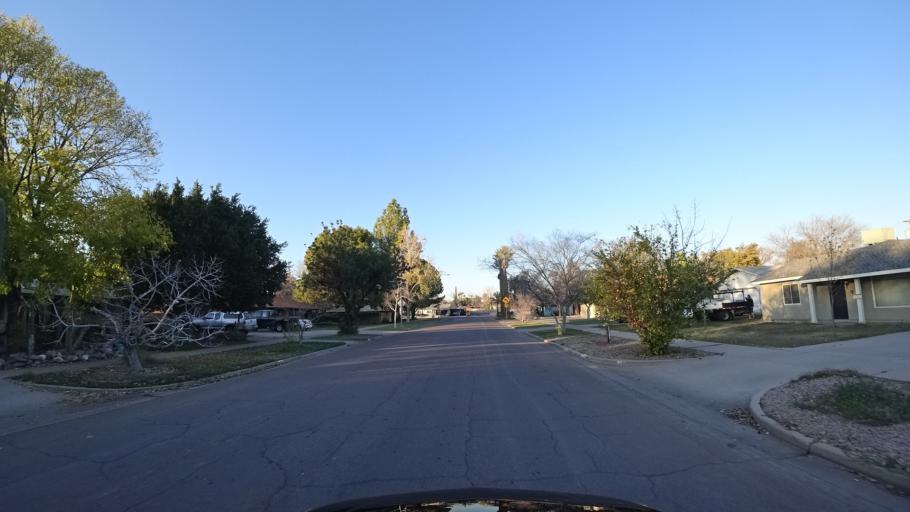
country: US
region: Arizona
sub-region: Maricopa County
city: Mesa
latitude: 33.4300
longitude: -111.8371
